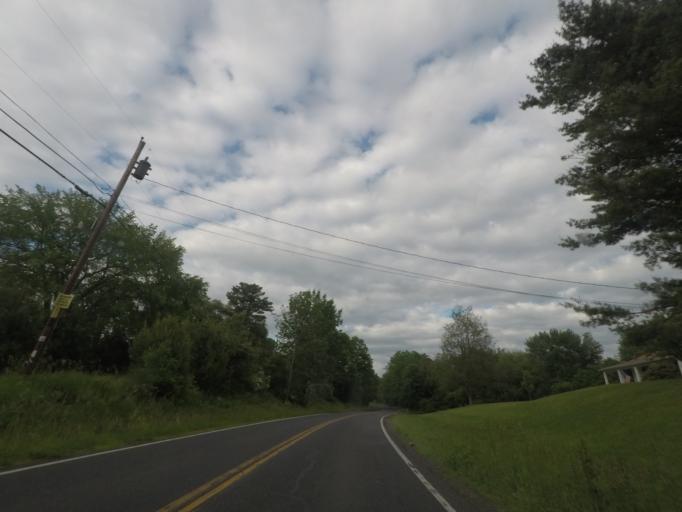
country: US
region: New York
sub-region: Ulster County
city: Plattekill
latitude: 41.6113
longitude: -74.1124
